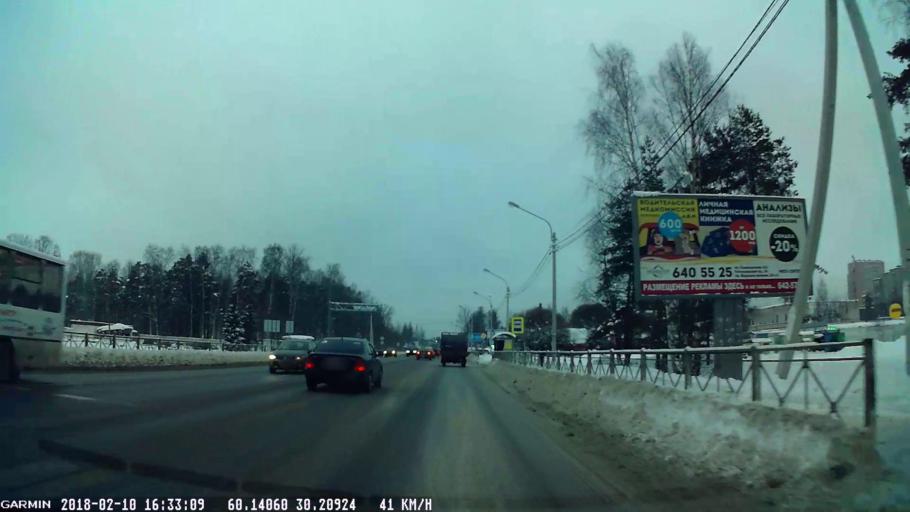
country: RU
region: Leningrad
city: Sertolovo
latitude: 60.1412
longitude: 30.2084
